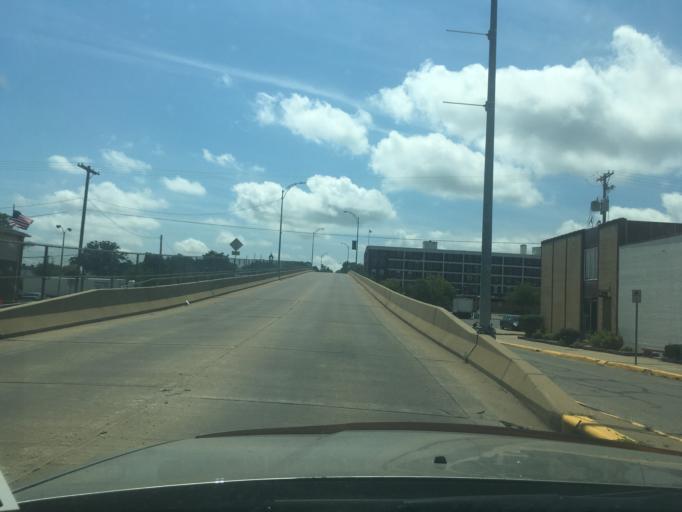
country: US
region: Kansas
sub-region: Atchison County
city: Atchison
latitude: 39.5618
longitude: -95.1192
